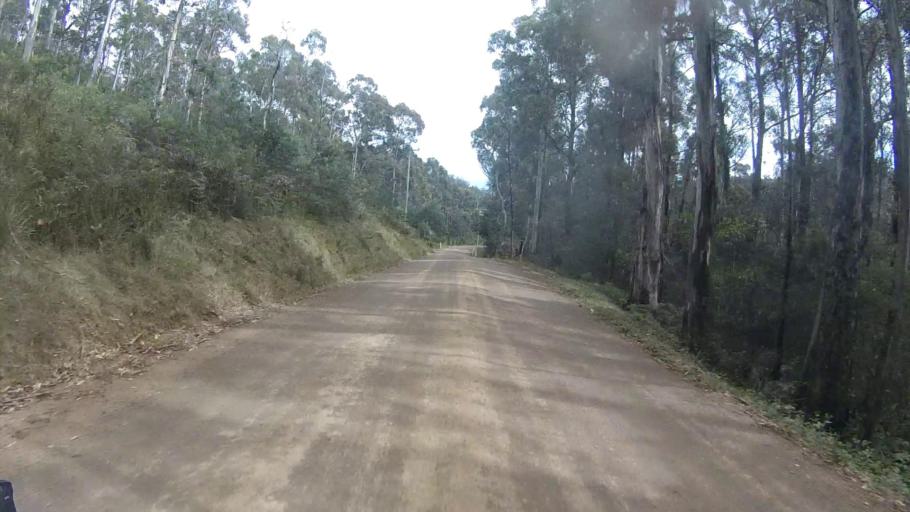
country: AU
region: Tasmania
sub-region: Sorell
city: Sorell
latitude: -42.7687
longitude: 147.8064
